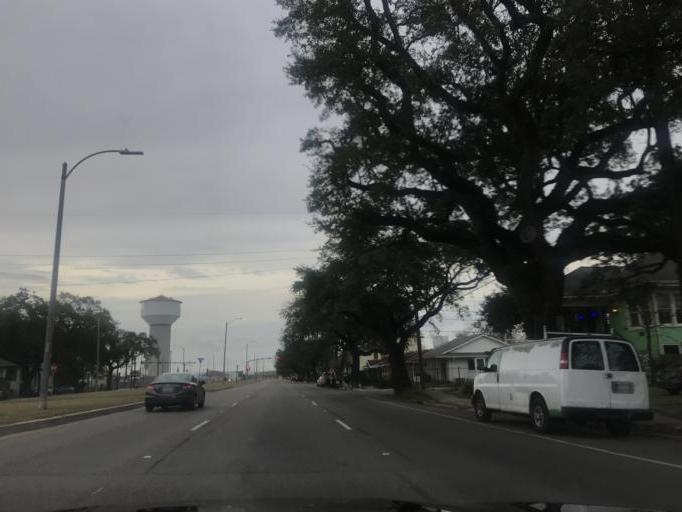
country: US
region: Louisiana
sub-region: Jefferson Parish
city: Jefferson
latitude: 29.9585
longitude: -90.1235
